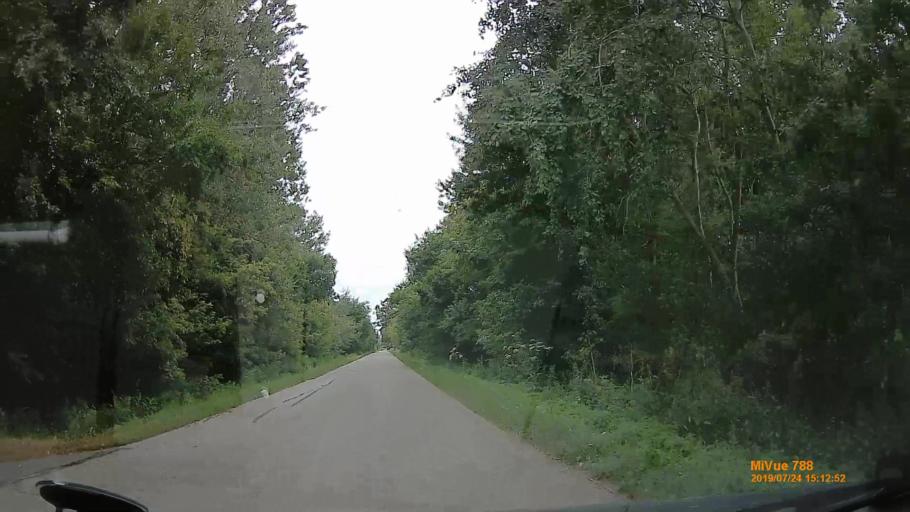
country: HU
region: Szabolcs-Szatmar-Bereg
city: Tarpa
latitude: 48.2007
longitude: 22.5047
